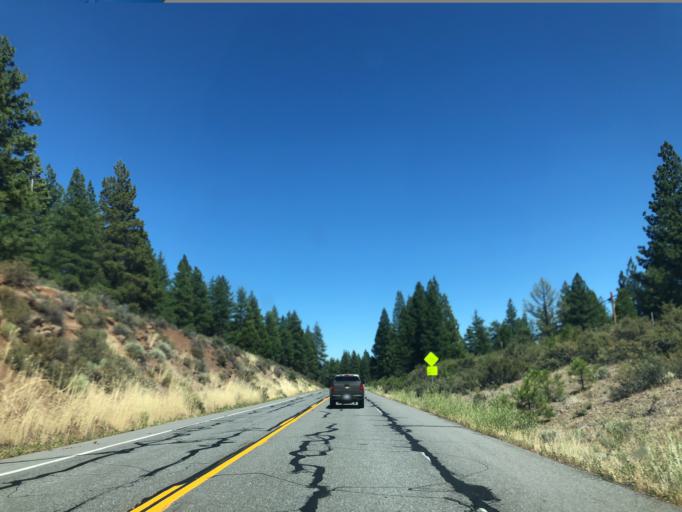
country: US
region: California
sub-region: Lassen County
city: Susanville
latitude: 40.4149
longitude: -120.7303
